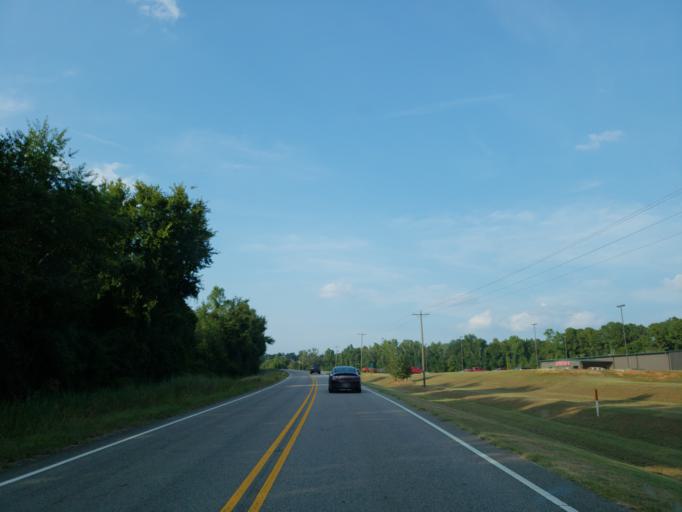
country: US
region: Alabama
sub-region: Greene County
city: Eutaw
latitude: 32.9732
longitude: -87.7917
